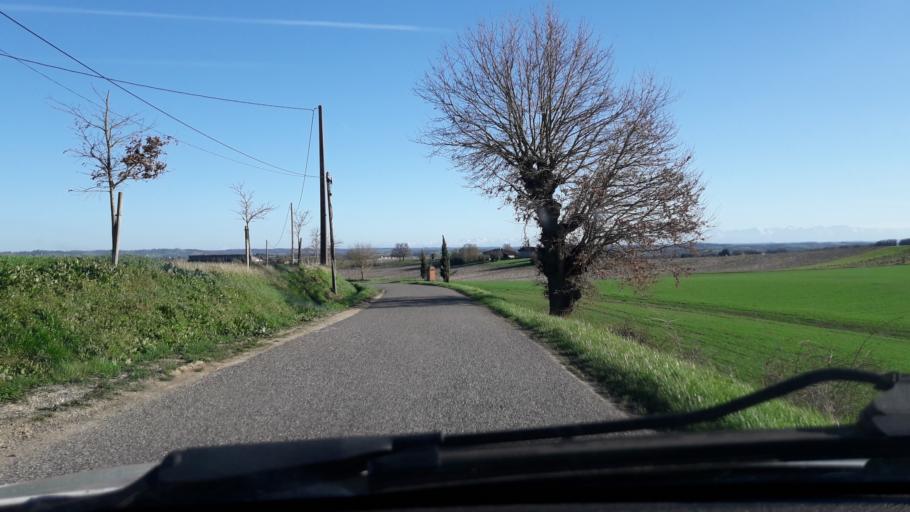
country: FR
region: Midi-Pyrenees
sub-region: Departement du Gers
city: Samatan
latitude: 43.5845
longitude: 1.0004
